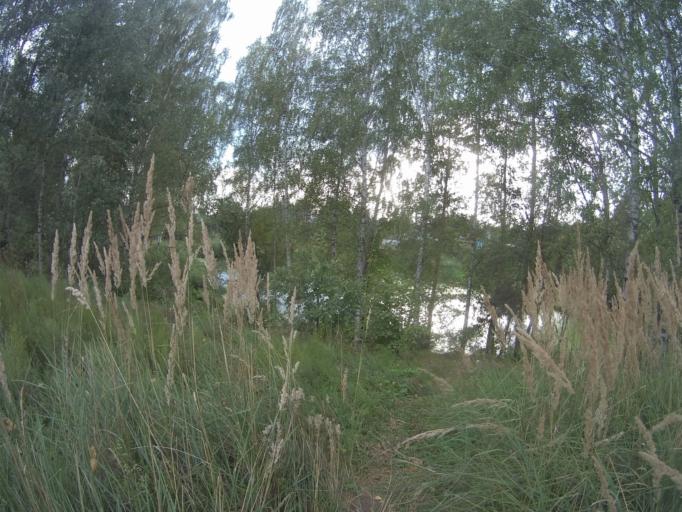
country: RU
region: Vladimir
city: Vorsha
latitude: 56.0138
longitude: 40.1829
